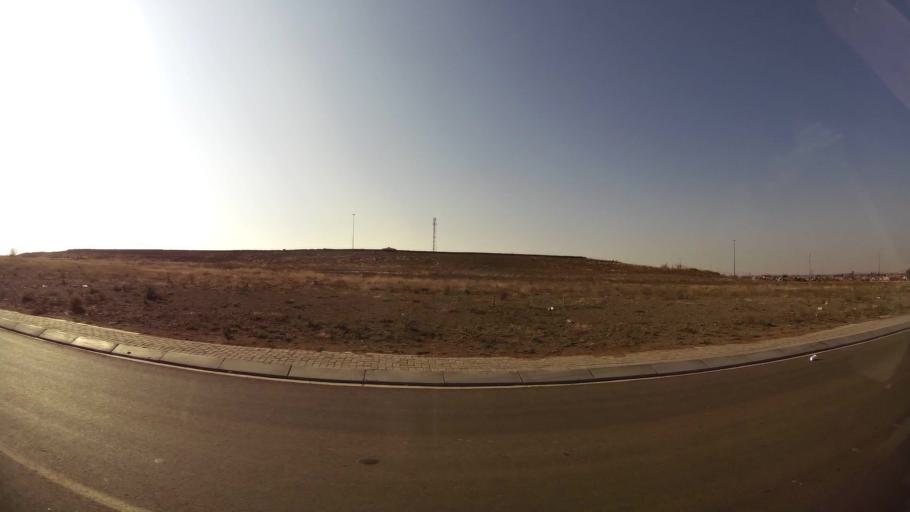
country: ZA
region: Orange Free State
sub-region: Mangaung Metropolitan Municipality
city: Bloemfontein
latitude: -29.1958
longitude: 26.2176
